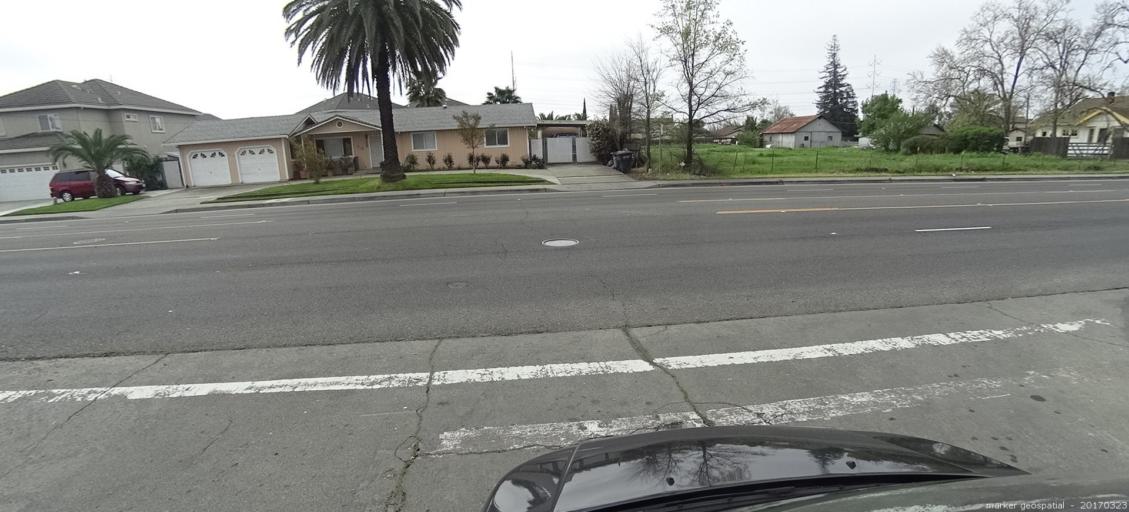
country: US
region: California
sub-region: Sacramento County
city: Florin
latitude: 38.5107
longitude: -121.4211
